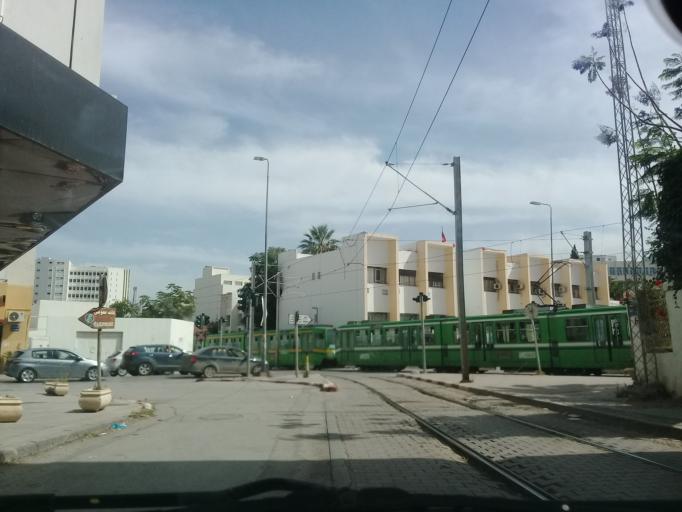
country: TN
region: Tunis
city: Tunis
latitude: 36.8178
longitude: 10.1816
